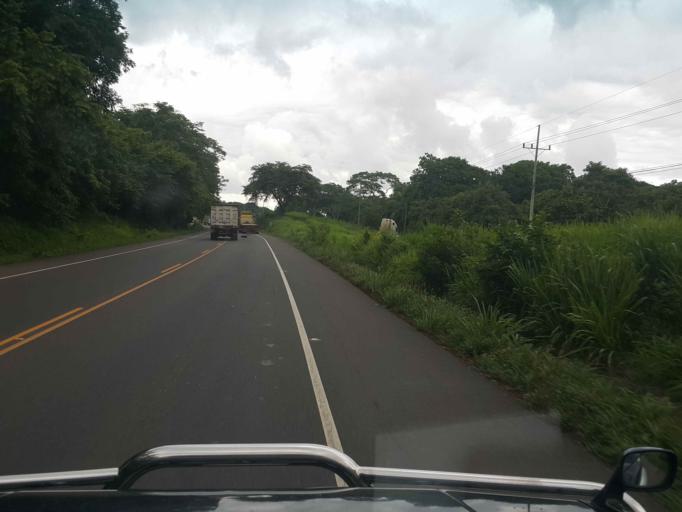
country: CR
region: Puntarenas
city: Esparza
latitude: 9.8985
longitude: -84.6571
